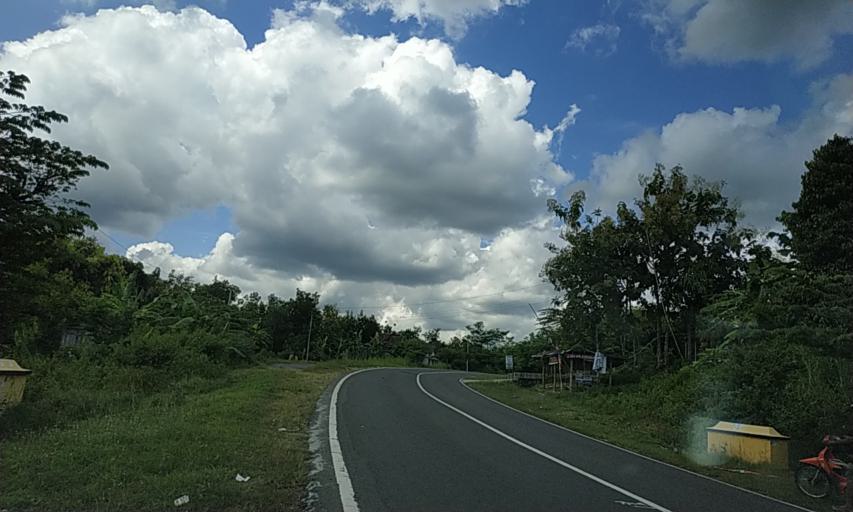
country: ID
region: East Java
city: Krajan
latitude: -8.0444
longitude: 110.9479
